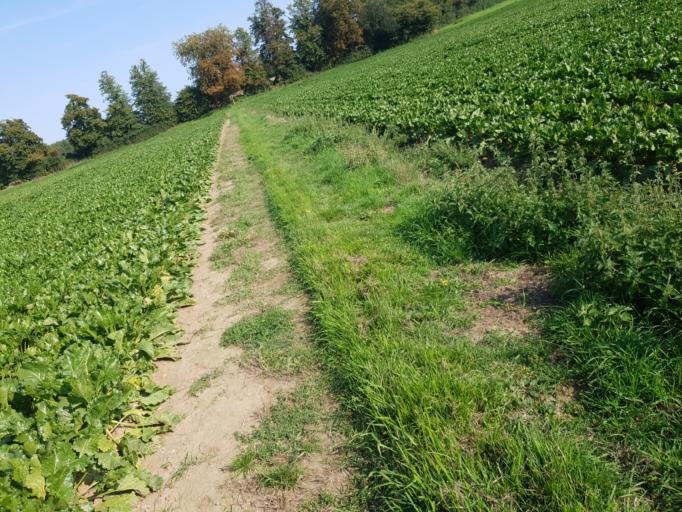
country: GB
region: England
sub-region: Suffolk
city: East Bergholt
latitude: 51.9497
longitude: 1.0104
